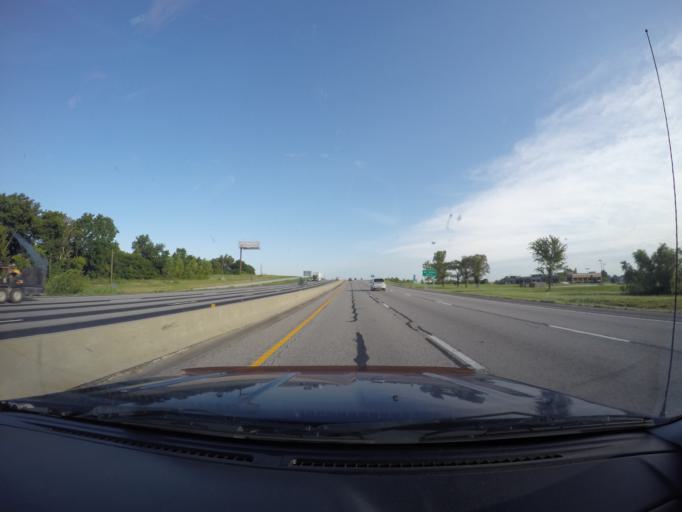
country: US
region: Missouri
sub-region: Platte County
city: Weatherby Lake
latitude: 39.2824
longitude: -94.6759
